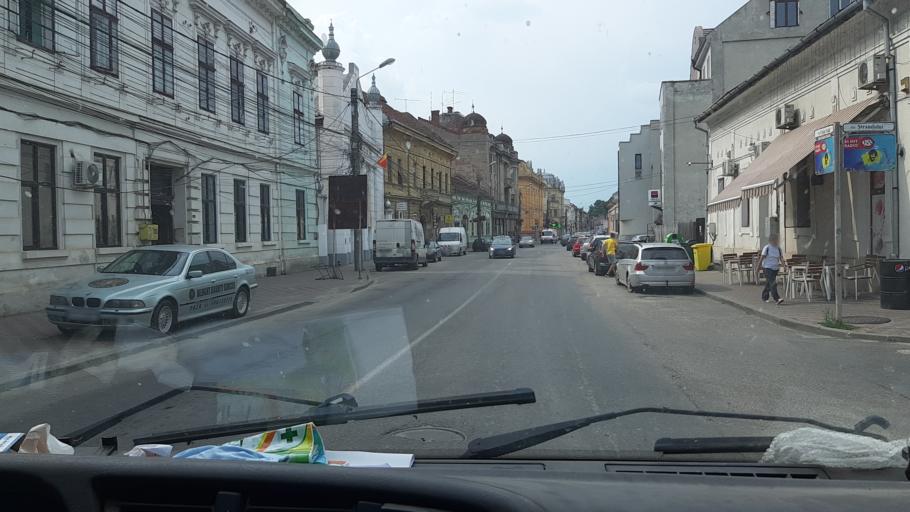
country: RO
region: Timis
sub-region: Municipiul Lugoj
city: Lugoj
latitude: 45.6813
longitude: 21.9033
